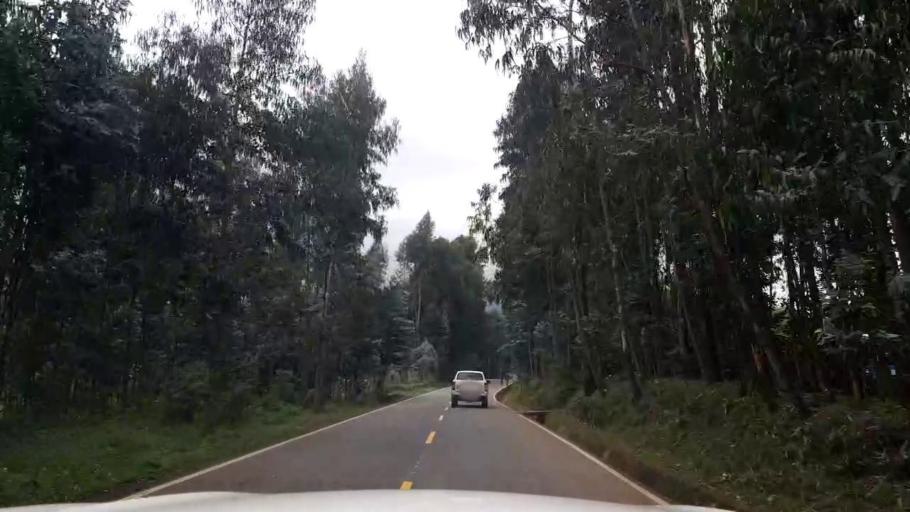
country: RW
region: Northern Province
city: Musanze
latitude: -1.4377
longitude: 29.5483
